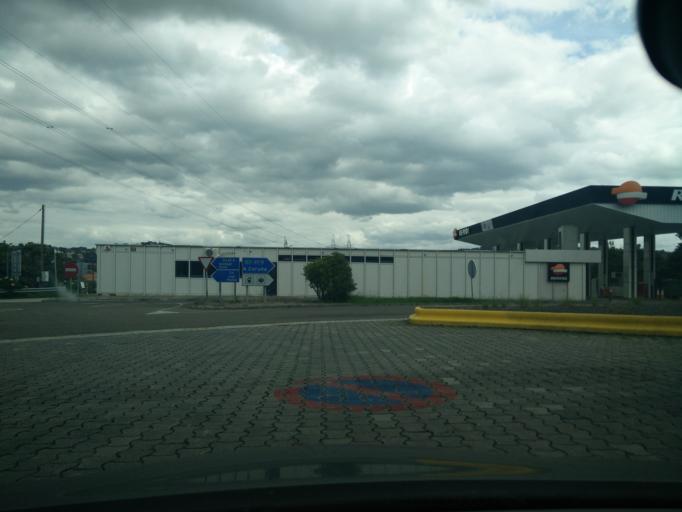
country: ES
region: Galicia
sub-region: Provincia da Coruna
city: Cambre
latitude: 43.3123
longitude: -8.3658
